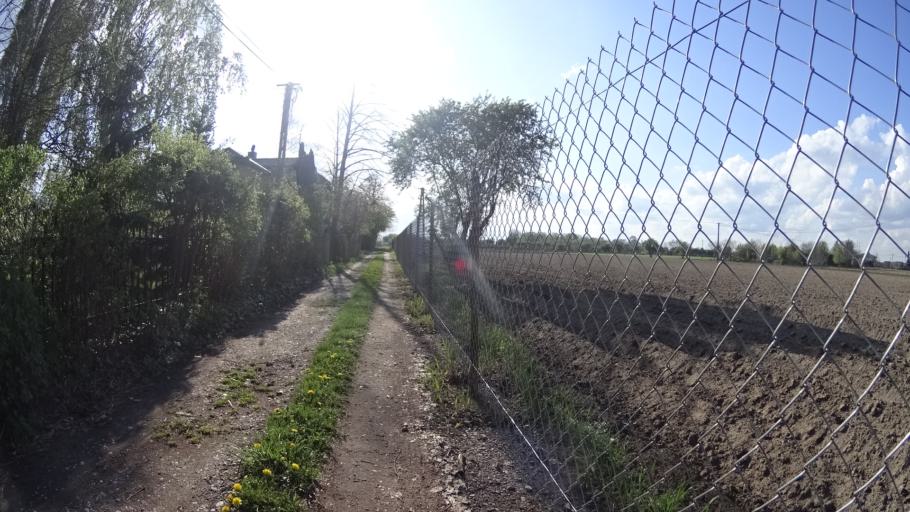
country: PL
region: Masovian Voivodeship
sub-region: Powiat warszawski zachodni
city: Jozefow
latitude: 52.2314
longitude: 20.7328
